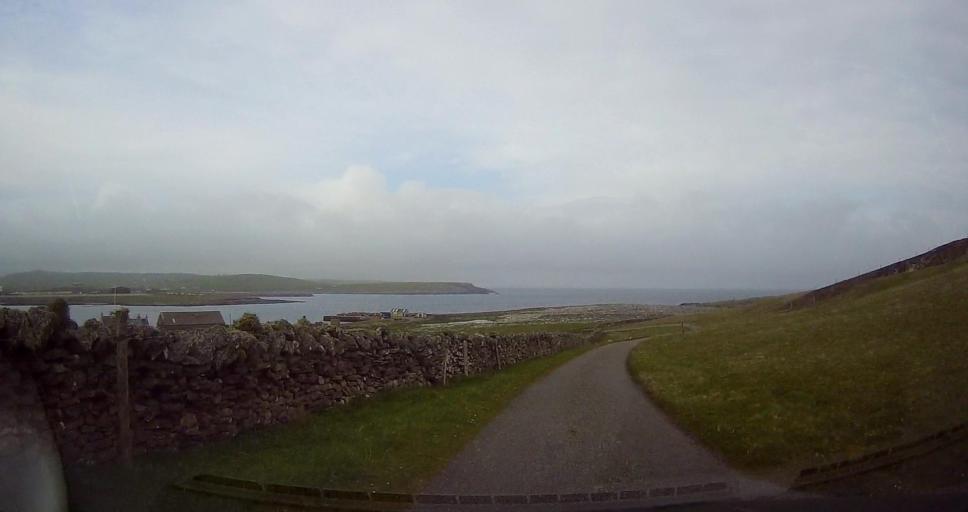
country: GB
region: Scotland
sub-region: Shetland Islands
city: Sandwick
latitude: 59.8705
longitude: -1.2785
